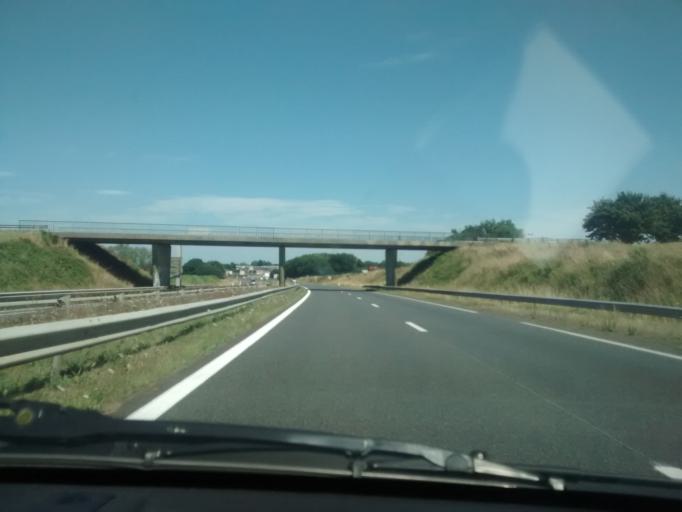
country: FR
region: Brittany
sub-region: Departement des Cotes-d'Armor
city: Tremuson
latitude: 48.5229
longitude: -2.8746
